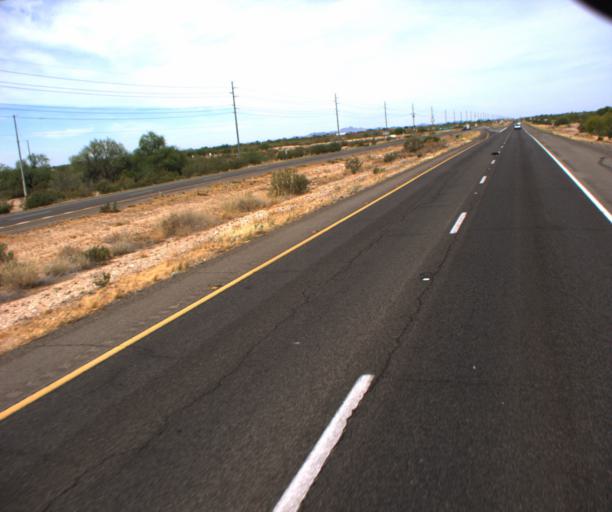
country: US
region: Arizona
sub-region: Maricopa County
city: Sun City West
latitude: 33.7386
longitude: -112.4780
